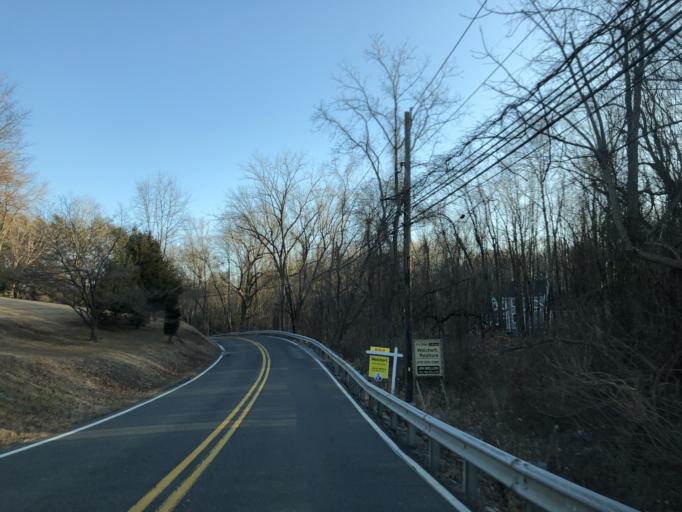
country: US
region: Pennsylvania
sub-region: Delaware County
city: Chester Heights
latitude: 39.8640
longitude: -75.5059
